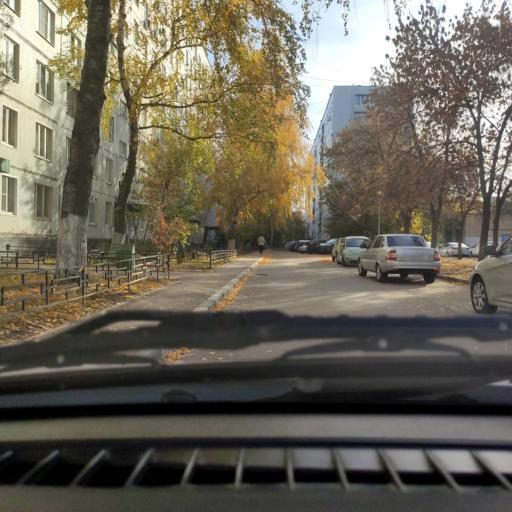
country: RU
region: Samara
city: Tol'yatti
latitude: 53.5346
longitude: 49.2762
